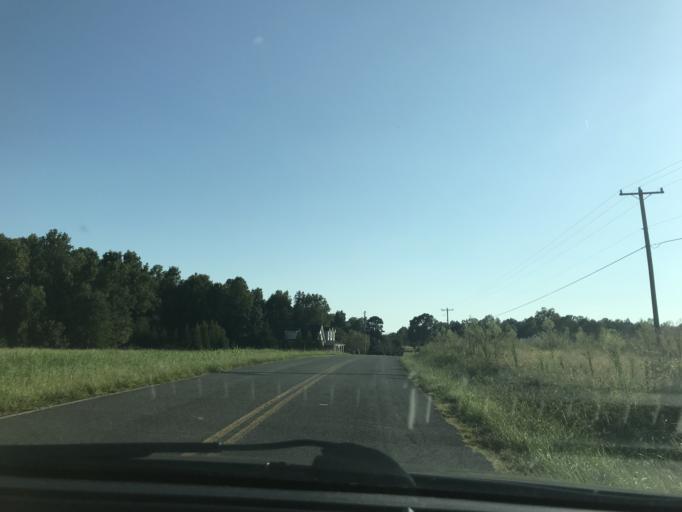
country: US
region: North Carolina
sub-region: Cleveland County
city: Boiling Springs
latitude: 35.1583
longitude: -81.7383
